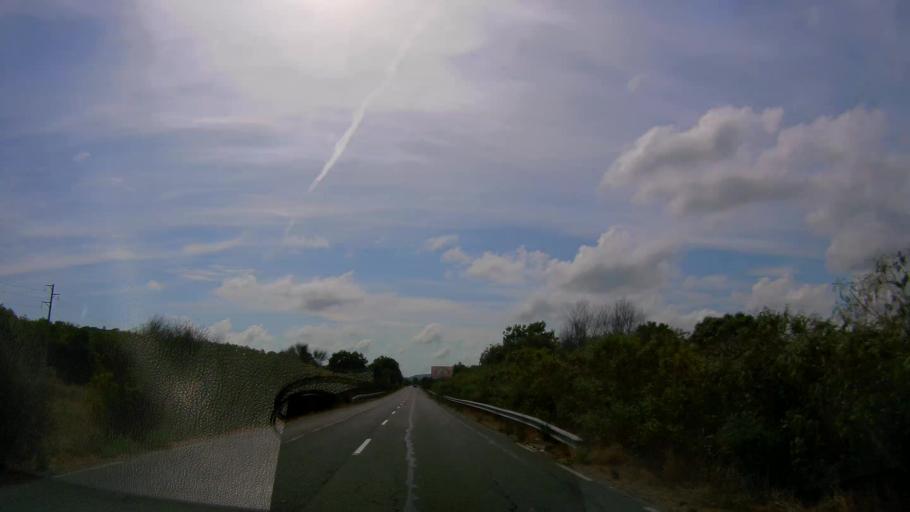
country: BG
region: Burgas
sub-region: Obshtina Sozopol
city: Sozopol
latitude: 42.3747
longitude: 27.6826
